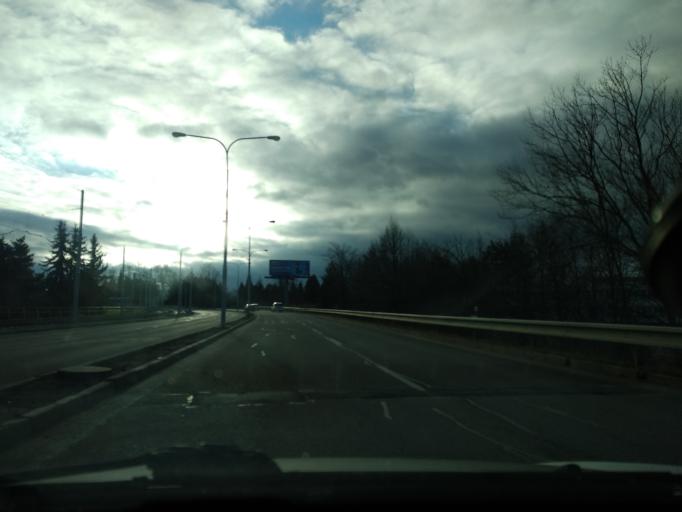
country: CZ
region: South Moravian
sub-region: Mesto Brno
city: Brno
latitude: 49.2176
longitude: 16.6163
